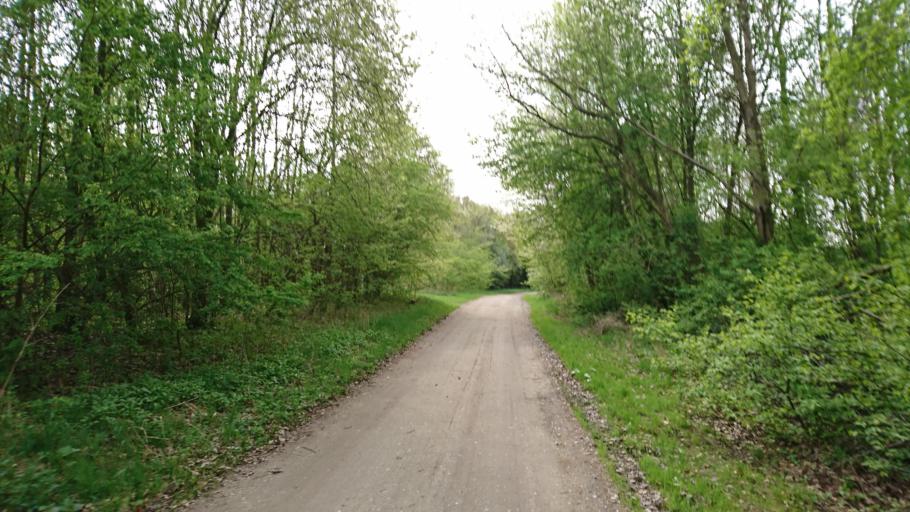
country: DK
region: Capital Region
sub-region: Ballerup Kommune
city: Ballerup
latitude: 55.7457
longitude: 12.3978
